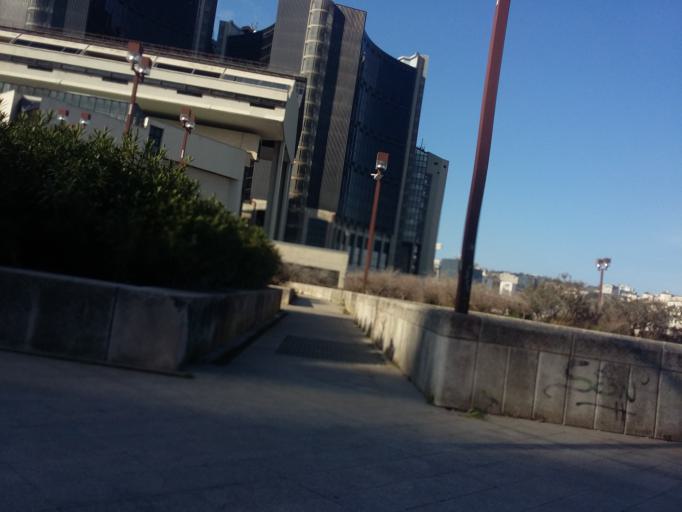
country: IT
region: Campania
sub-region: Provincia di Napoli
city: Napoli
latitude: 40.8585
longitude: 14.2845
